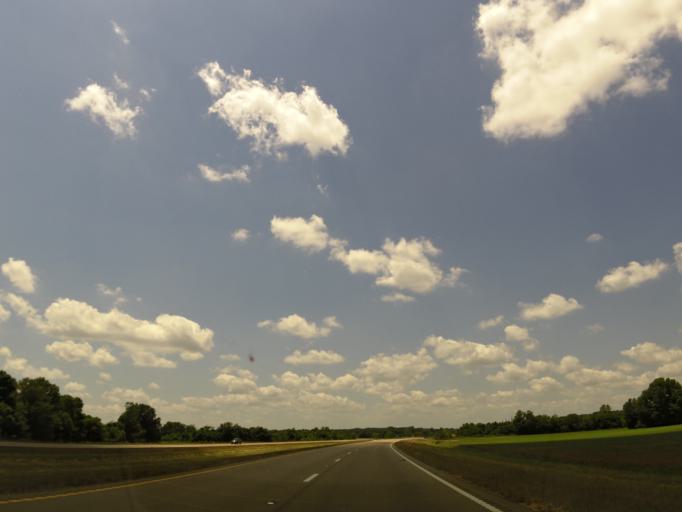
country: US
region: Mississippi
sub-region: Pontotoc County
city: Pontotoc
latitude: 34.2214
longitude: -88.8703
